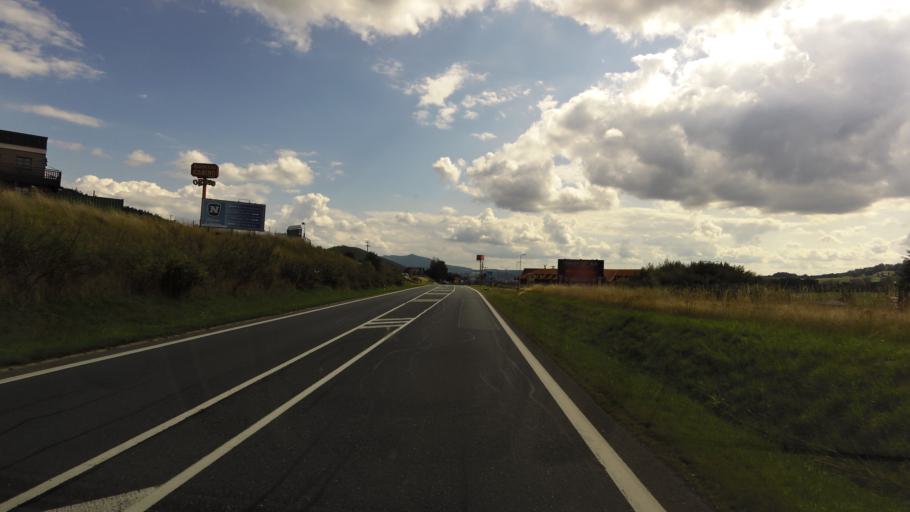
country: DE
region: Bavaria
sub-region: Upper Palatinate
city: Furth im Wald
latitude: 49.3537
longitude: 12.8534
